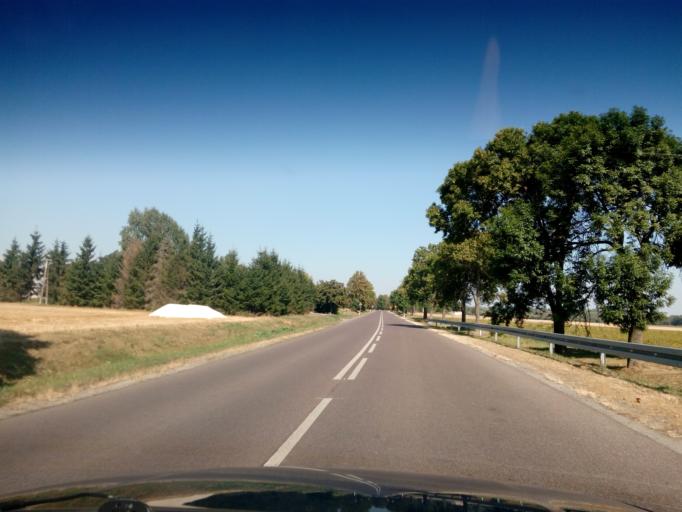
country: PL
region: Lublin Voivodeship
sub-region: Powiat hrubieszowski
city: Horodlo
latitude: 50.8516
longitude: 24.1199
